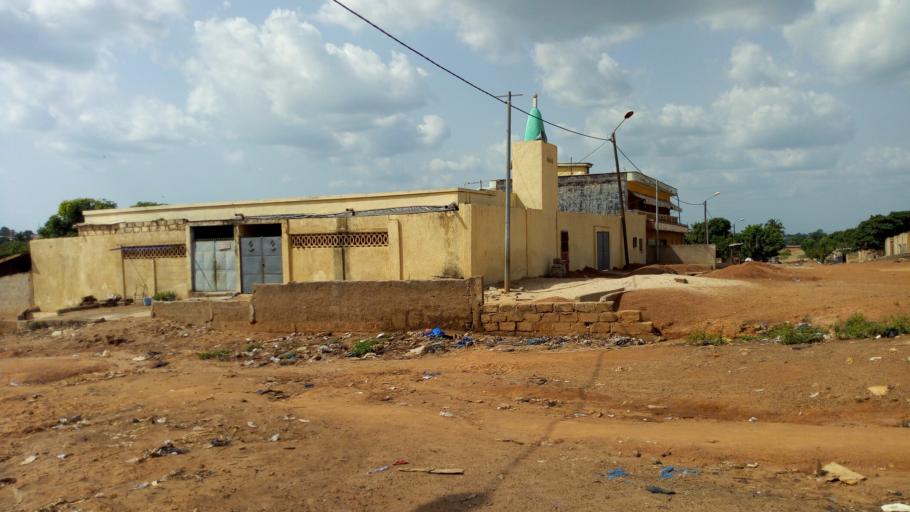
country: CI
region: Vallee du Bandama
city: Bouake
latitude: 7.7231
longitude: -5.0367
